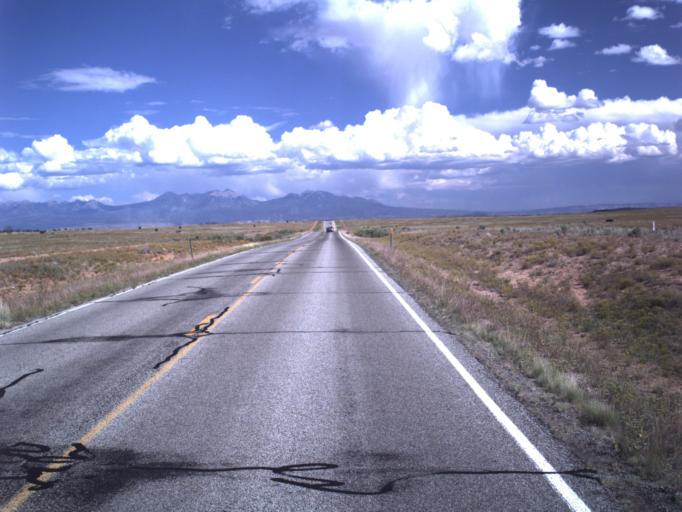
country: US
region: Utah
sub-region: Grand County
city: Moab
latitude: 38.5497
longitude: -109.7799
